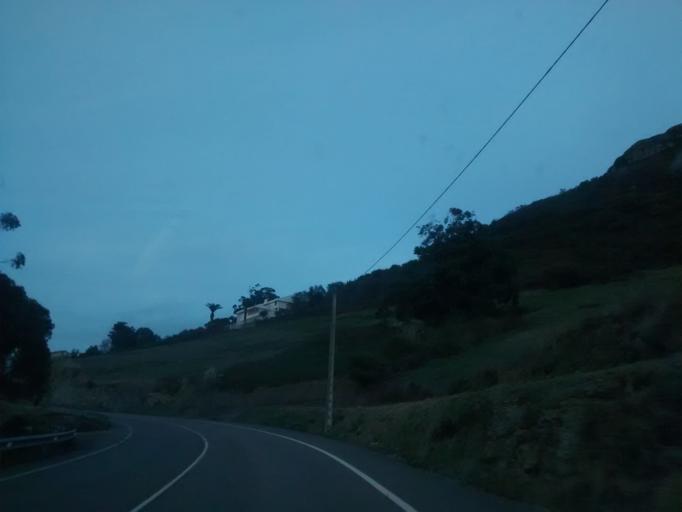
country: ES
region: Cantabria
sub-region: Provincia de Cantabria
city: Santa Cruz de Bezana
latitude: 43.4395
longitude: -3.9493
